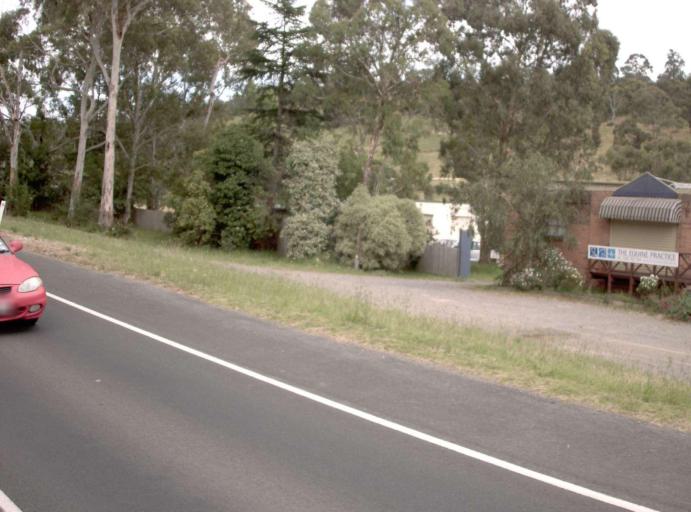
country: AU
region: Victoria
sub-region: Yarra Ranges
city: Lilydale
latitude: -37.7435
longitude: 145.3733
